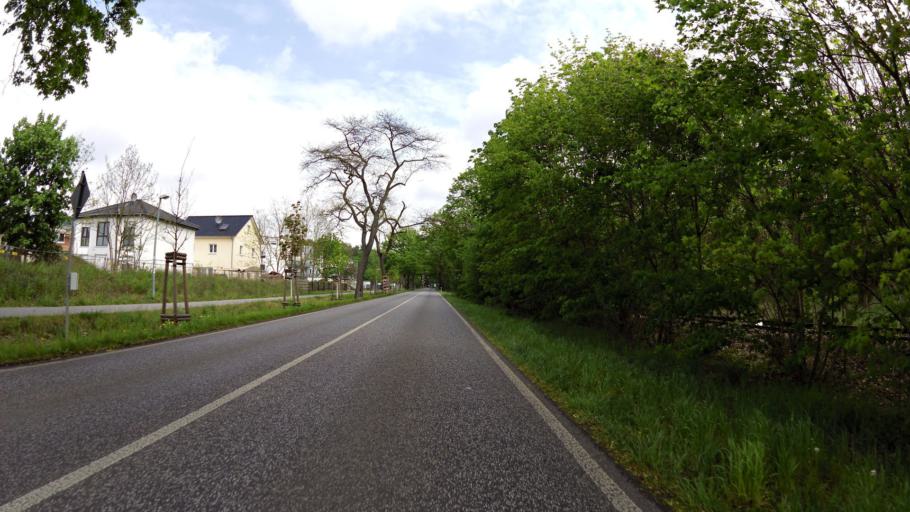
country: DE
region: Brandenburg
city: Konigs Wusterhausen
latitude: 52.2812
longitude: 13.6106
